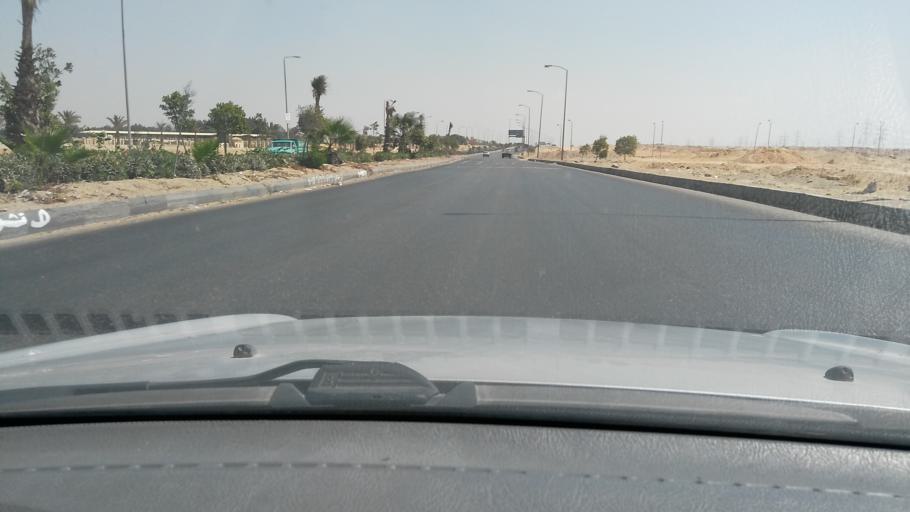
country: EG
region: Al Jizah
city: Madinat Sittah Uktubar
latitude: 29.9576
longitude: 30.9630
